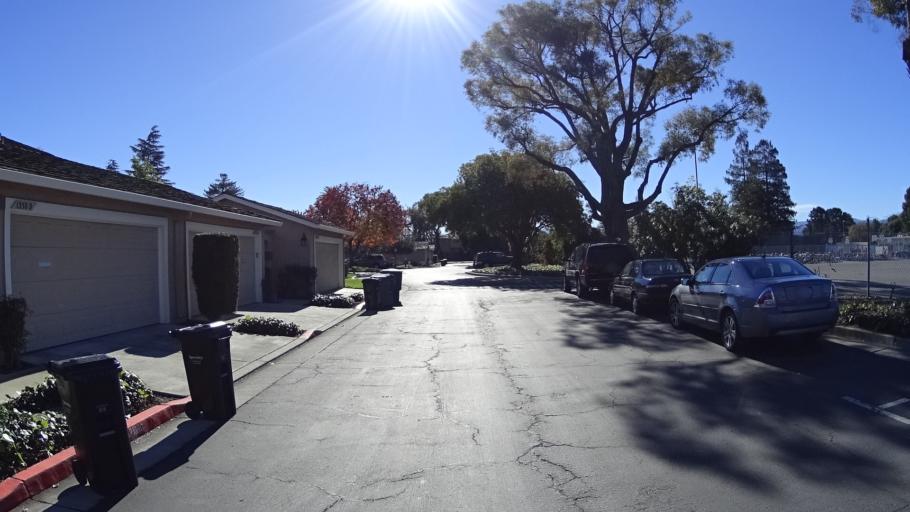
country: US
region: California
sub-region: Santa Clara County
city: Sunnyvale
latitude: 37.3500
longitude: -122.0057
